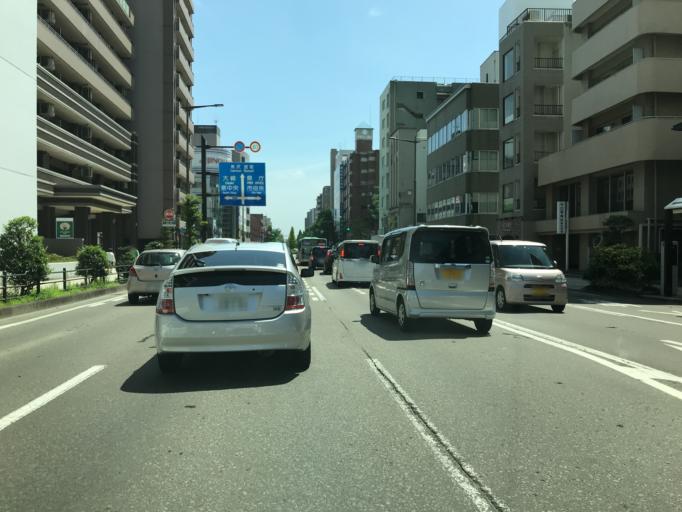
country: JP
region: Miyagi
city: Sendai-shi
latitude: 38.2720
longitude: 140.8677
